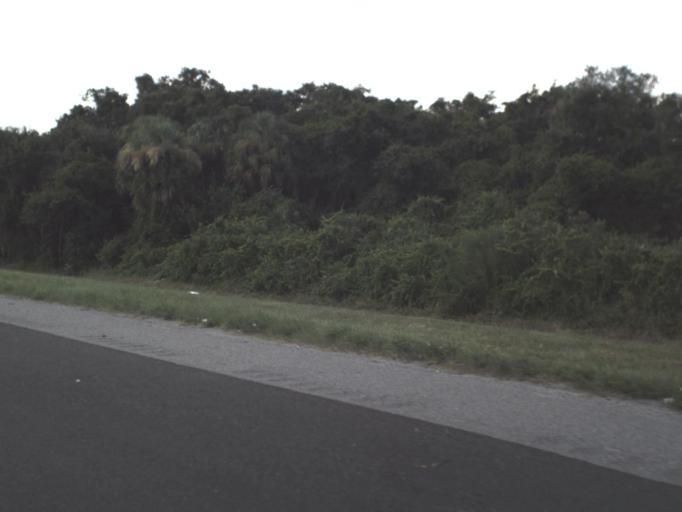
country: US
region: Florida
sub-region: Hillsborough County
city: Riverview
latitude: 27.8540
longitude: -82.3468
